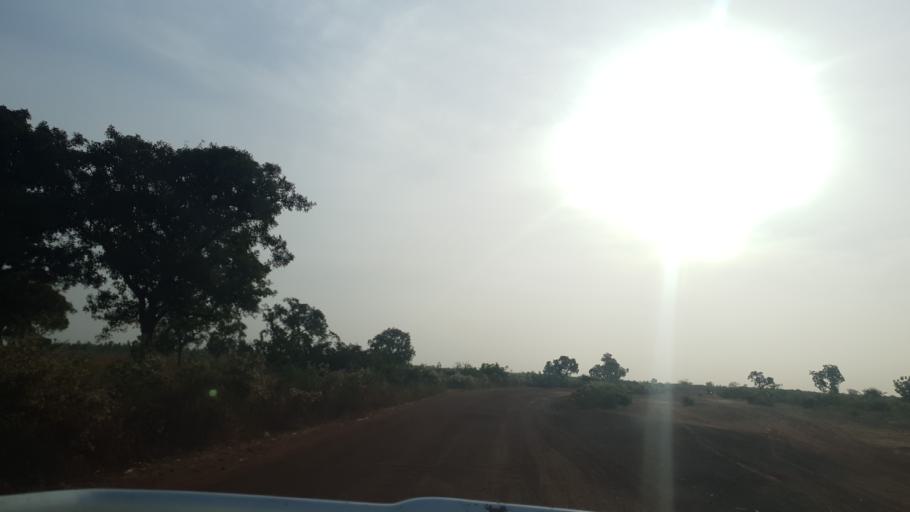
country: ML
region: Koulikoro
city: Dioila
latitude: 12.7695
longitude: -6.9259
